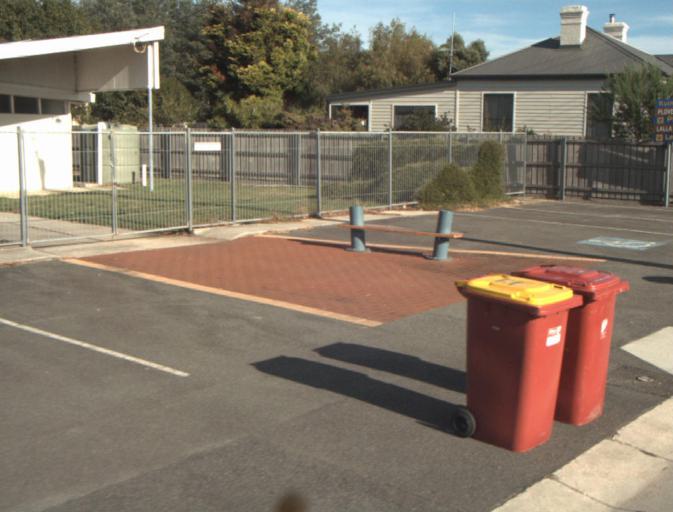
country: AU
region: Tasmania
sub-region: Launceston
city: Mayfield
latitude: -41.2517
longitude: 147.2166
